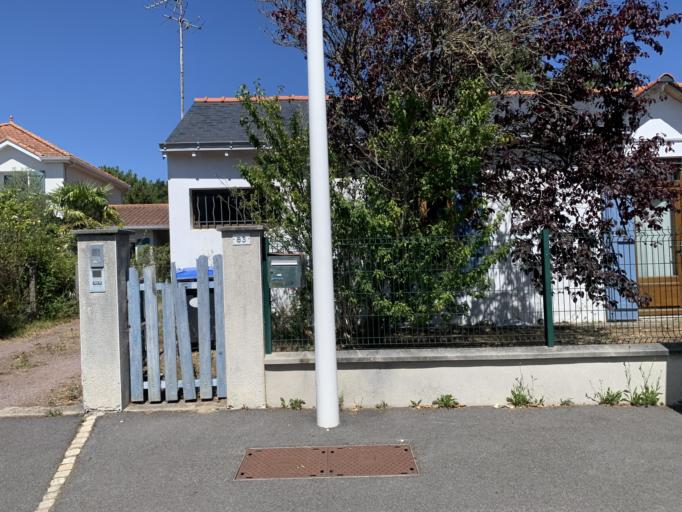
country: FR
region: Pays de la Loire
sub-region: Departement de la Loire-Atlantique
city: Pornichet
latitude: 47.2570
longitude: -2.3256
